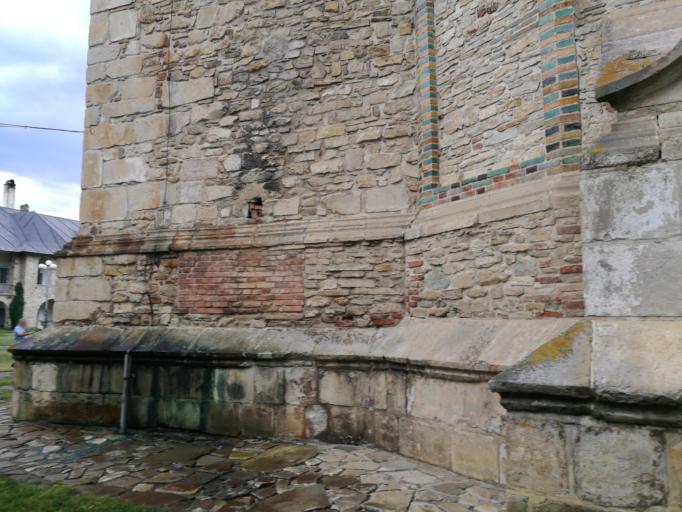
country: RO
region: Neamt
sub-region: Comuna Vanatori Neamt
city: Nemtisor
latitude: 47.2636
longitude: 26.2097
